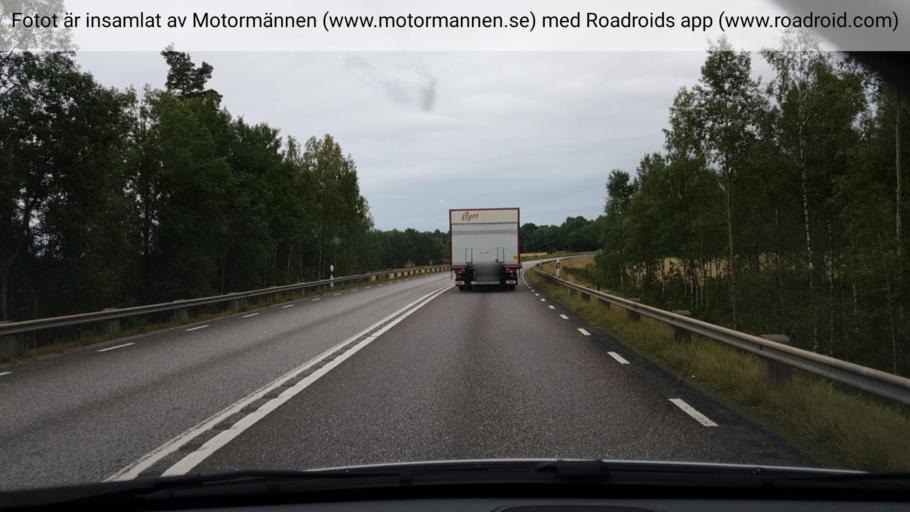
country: SE
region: Vaestra Goetaland
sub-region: Karlsborgs Kommun
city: Karlsborg
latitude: 58.5021
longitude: 14.4632
